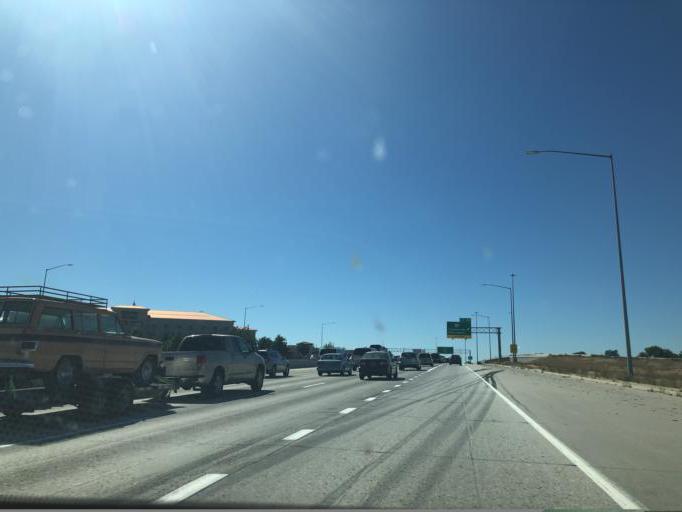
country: US
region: Idaho
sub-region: Ada County
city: Garden City
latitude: 43.5915
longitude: -116.2767
